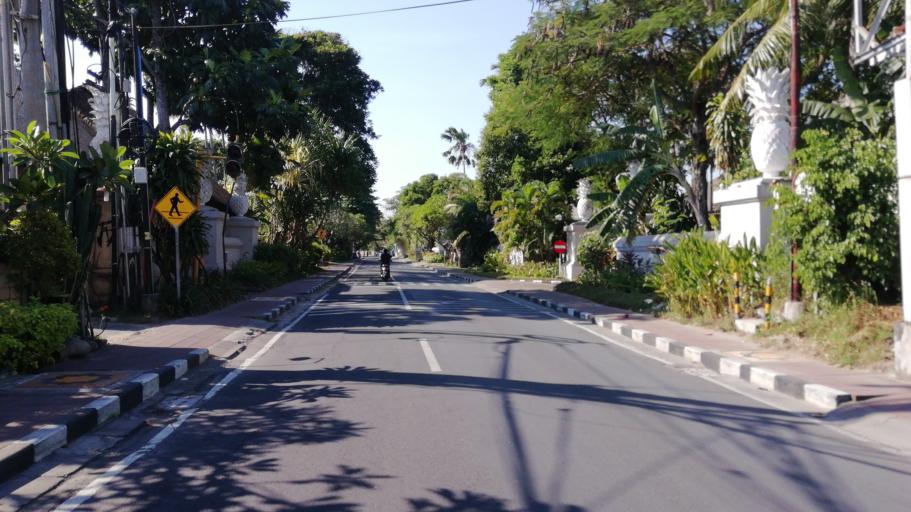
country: ID
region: Bali
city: Bualu
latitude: -8.7649
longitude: 115.2220
